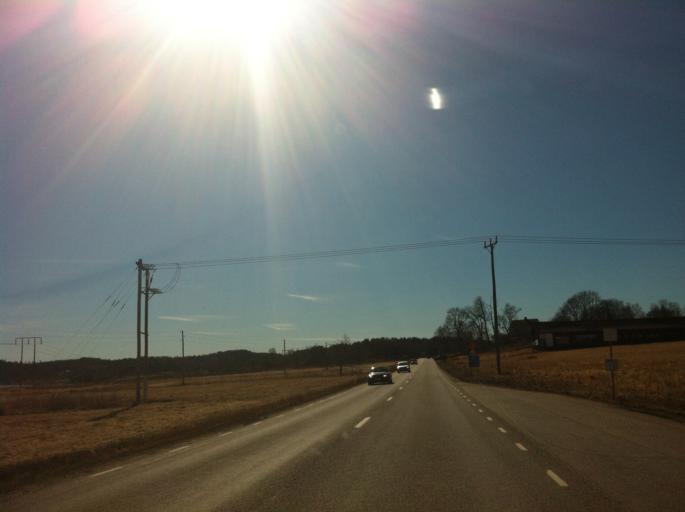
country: SE
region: Vaestra Goetaland
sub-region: Munkedals Kommun
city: Munkedal
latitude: 58.4262
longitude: 11.7194
